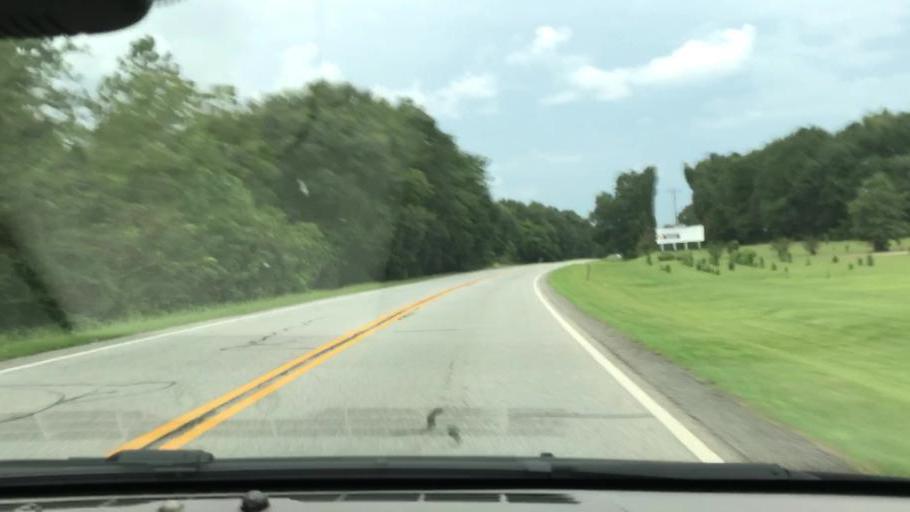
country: US
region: Georgia
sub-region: Early County
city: Blakely
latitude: 31.2805
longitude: -85.0750
